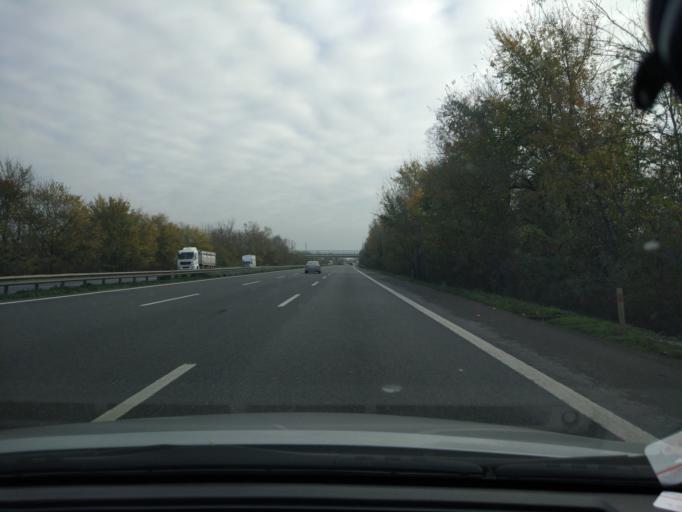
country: TR
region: Sakarya
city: Adapazari
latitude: 40.7196
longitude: 30.4465
